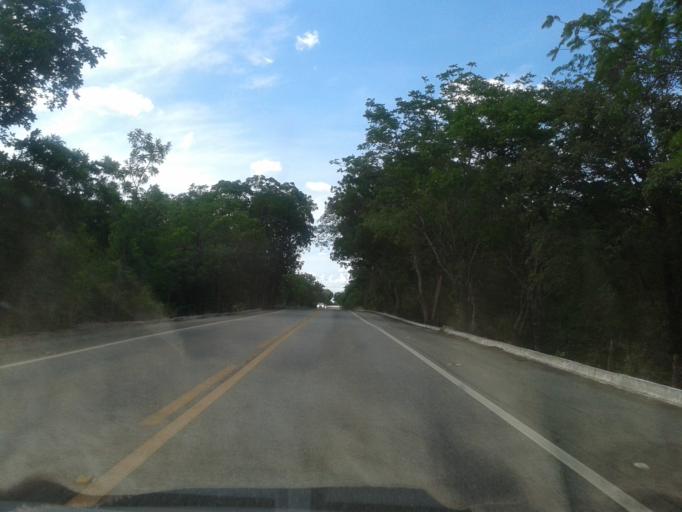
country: BR
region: Goias
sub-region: Itapuranga
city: Itapuranga
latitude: -15.4715
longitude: -50.3444
